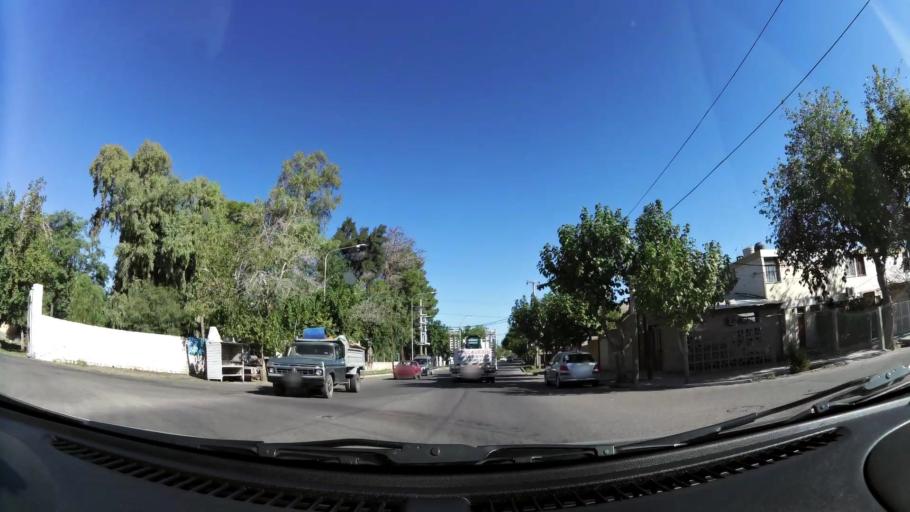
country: AR
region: San Juan
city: Villa Paula de Sarmiento
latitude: -31.5098
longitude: -68.5249
